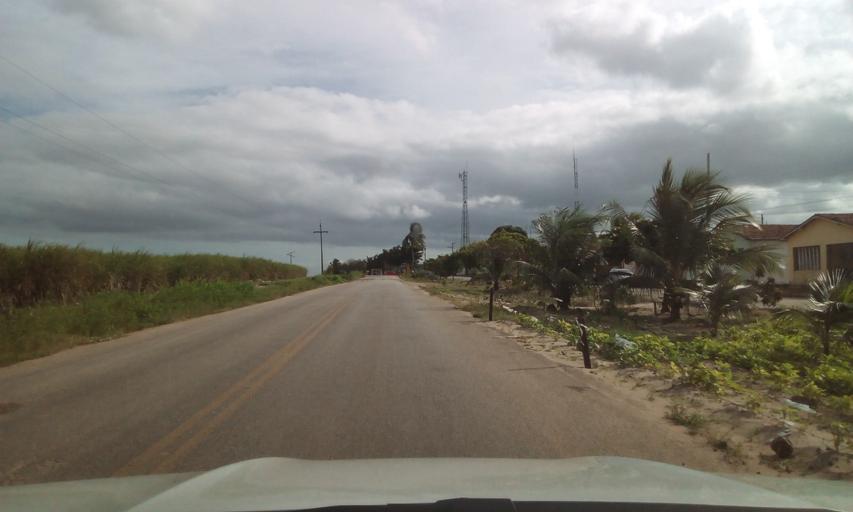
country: BR
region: Paraiba
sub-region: Santa Rita
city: Santa Rita
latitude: -6.9771
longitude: -34.9817
